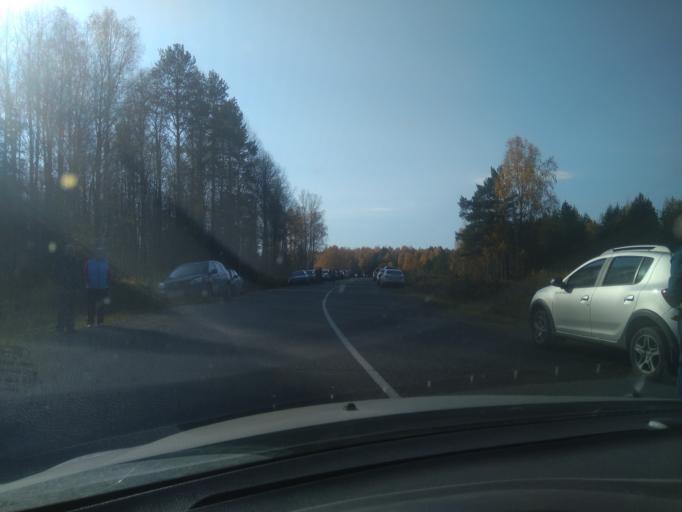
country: RU
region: Sverdlovsk
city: Mikhaylovsk
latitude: 56.5283
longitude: 59.2270
